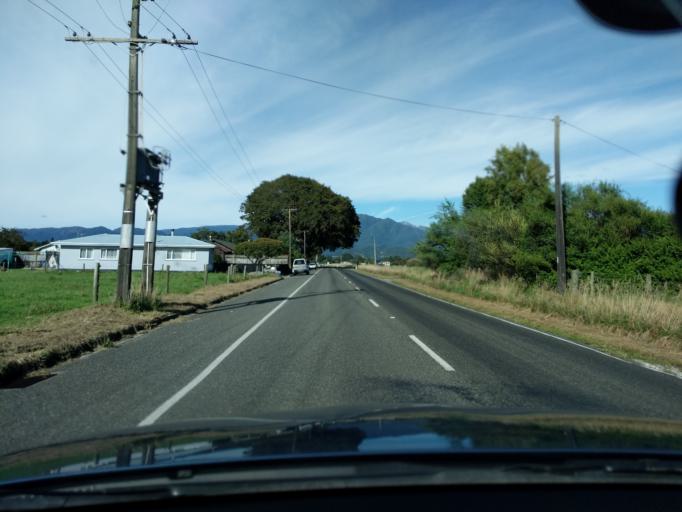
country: NZ
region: Tasman
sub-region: Tasman District
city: Takaka
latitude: -40.8506
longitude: 172.8314
